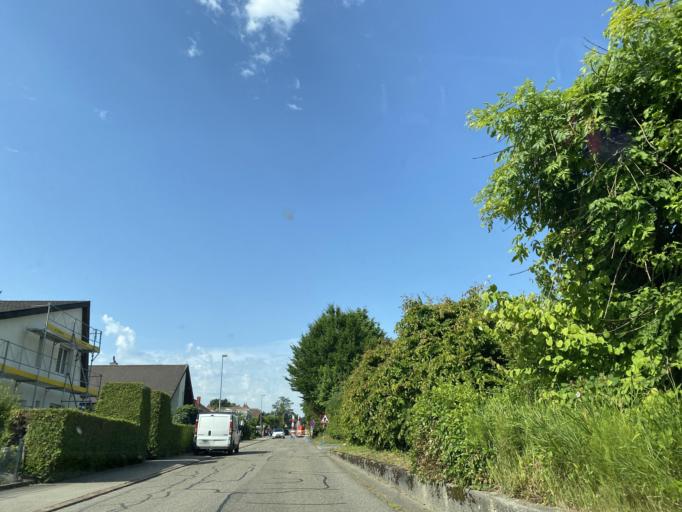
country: CH
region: Aargau
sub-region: Bezirk Zofingen
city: Rothrist
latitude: 47.3024
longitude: 7.8843
